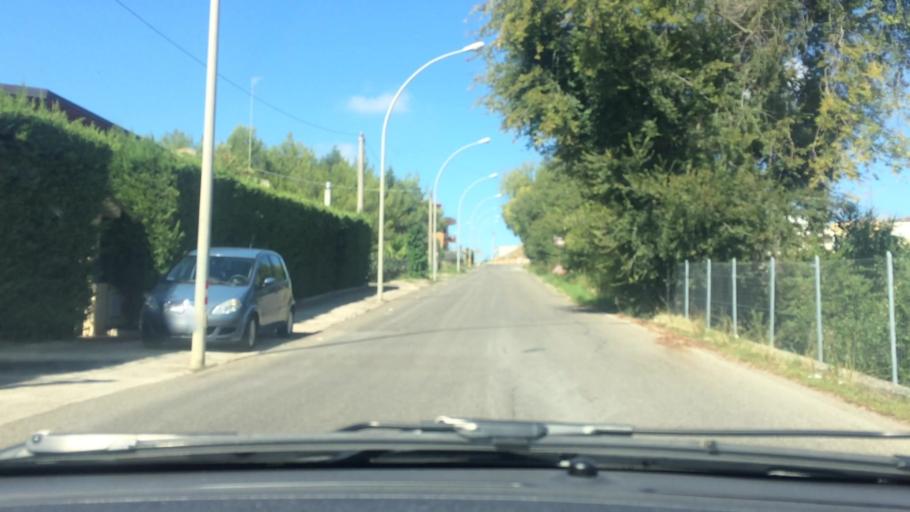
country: IT
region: Basilicate
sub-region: Provincia di Matera
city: Montescaglioso
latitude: 40.5434
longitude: 16.6704
